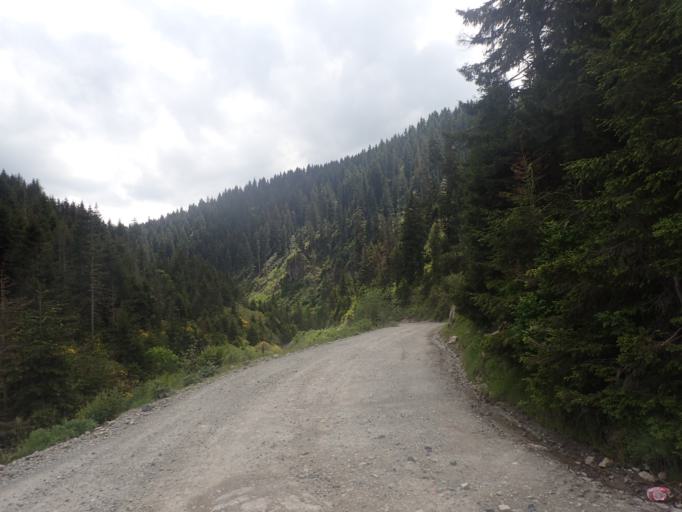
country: TR
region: Ordu
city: Topcam
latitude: 40.6823
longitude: 37.9466
